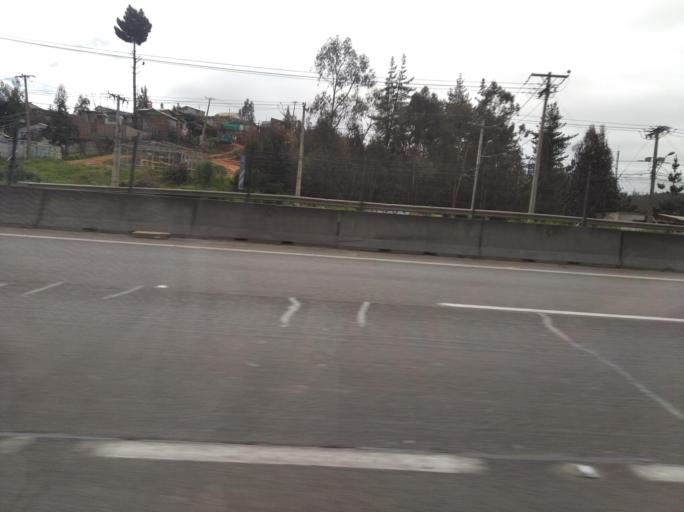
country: CL
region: Valparaiso
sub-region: Provincia de Valparaiso
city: Vina del Mar
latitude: -33.1102
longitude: -71.5589
